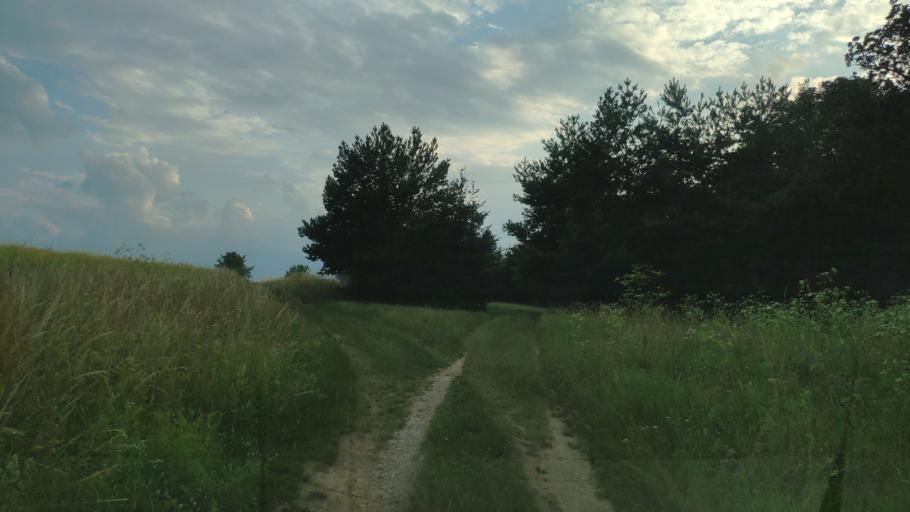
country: SK
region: Kosicky
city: Medzev
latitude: 48.7170
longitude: 20.9951
